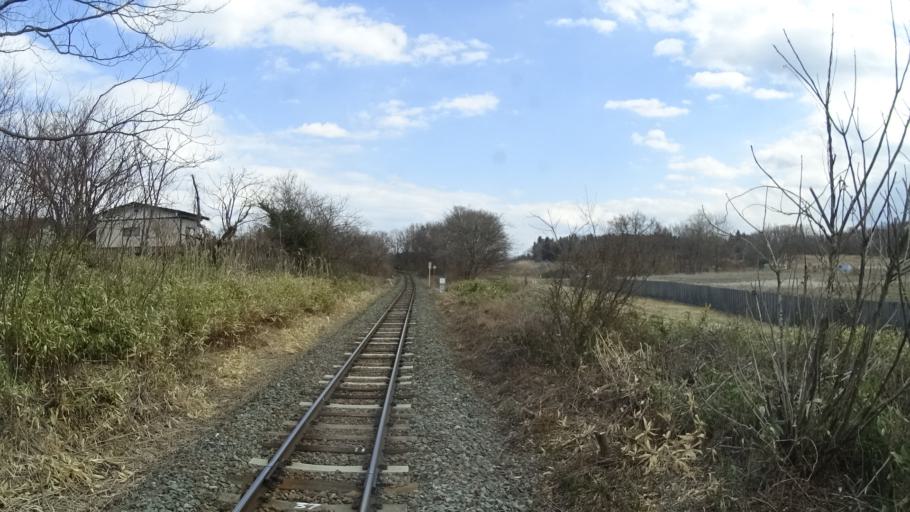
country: JP
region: Iwate
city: Hanamaki
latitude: 39.4080
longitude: 141.1952
